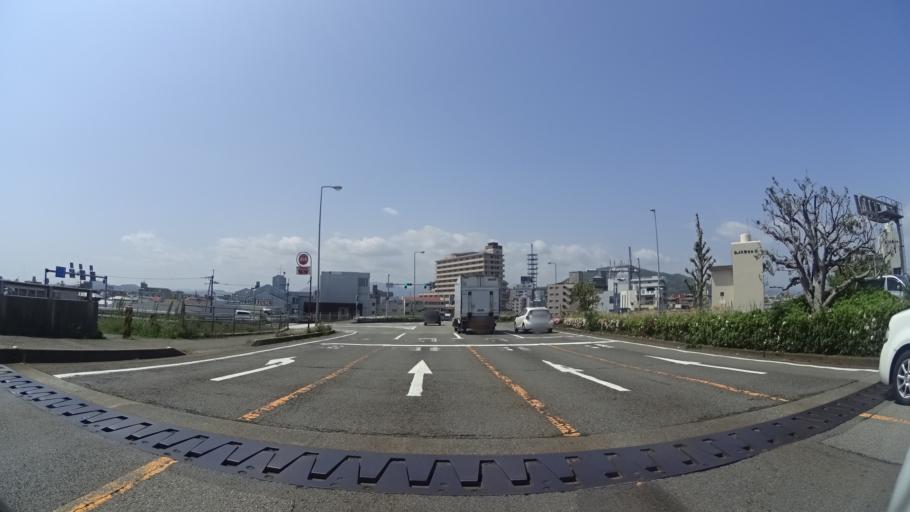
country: JP
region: Tokushima
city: Tokushima-shi
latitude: 34.0853
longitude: 134.5653
